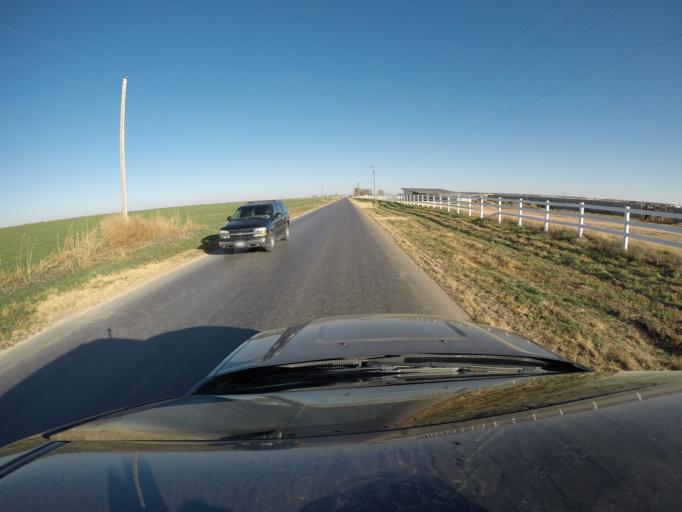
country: US
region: New Mexico
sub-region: Curry County
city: Clovis
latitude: 34.3029
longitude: -103.1413
